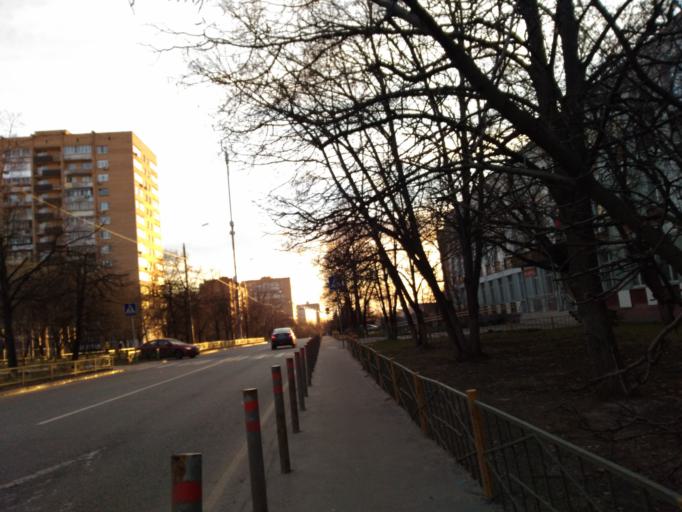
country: RU
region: Moskovskaya
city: Khoroshevo-Mnevniki
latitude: 55.7895
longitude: 37.4598
